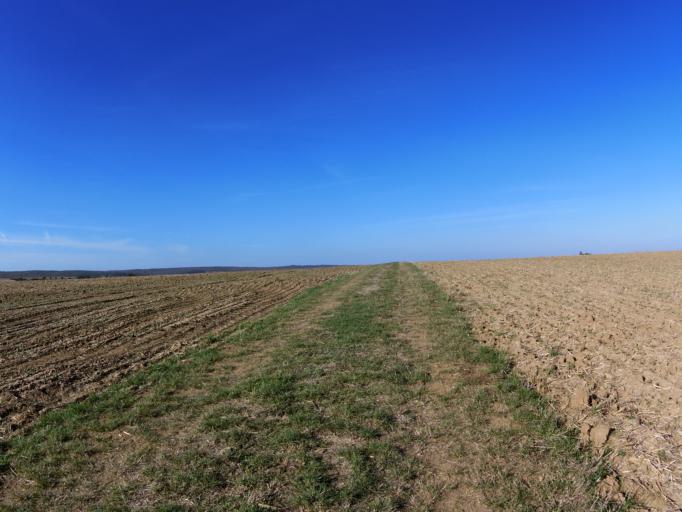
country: DE
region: Bavaria
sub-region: Regierungsbezirk Unterfranken
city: Geroldshausen
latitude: 49.6998
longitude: 9.9344
